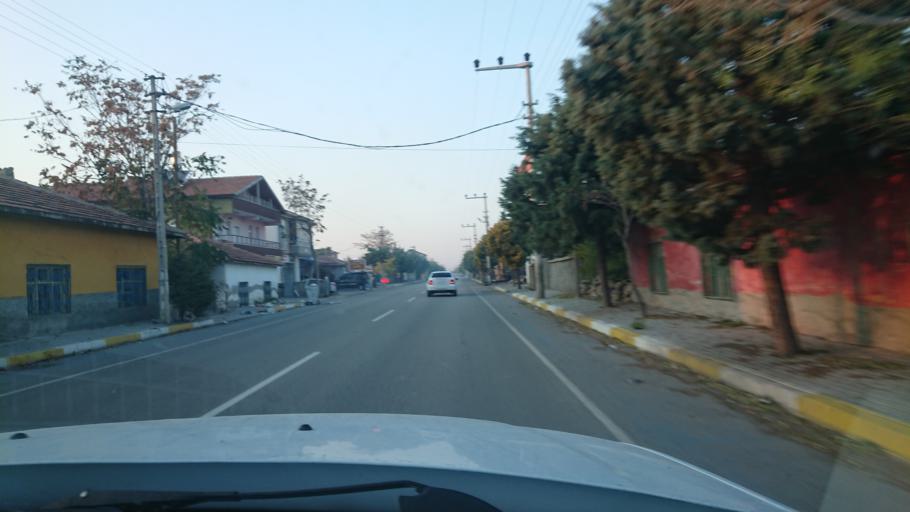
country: TR
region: Aksaray
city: Aksaray
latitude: 38.3030
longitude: 34.0699
